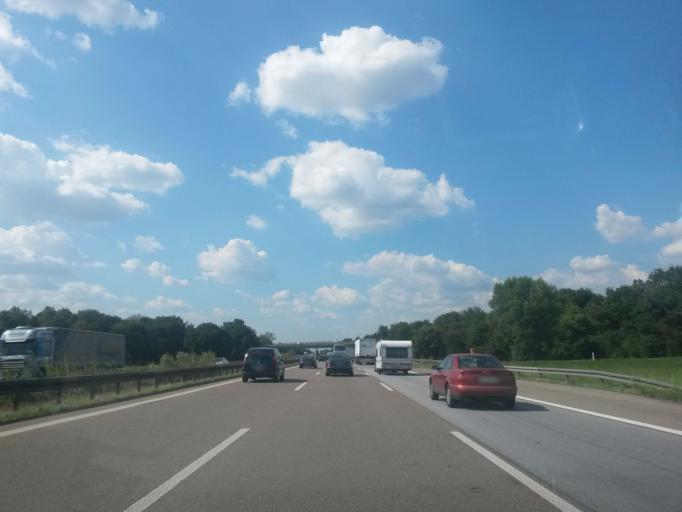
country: DE
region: Bavaria
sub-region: Upper Bavaria
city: Manching
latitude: 48.7078
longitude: 11.4862
